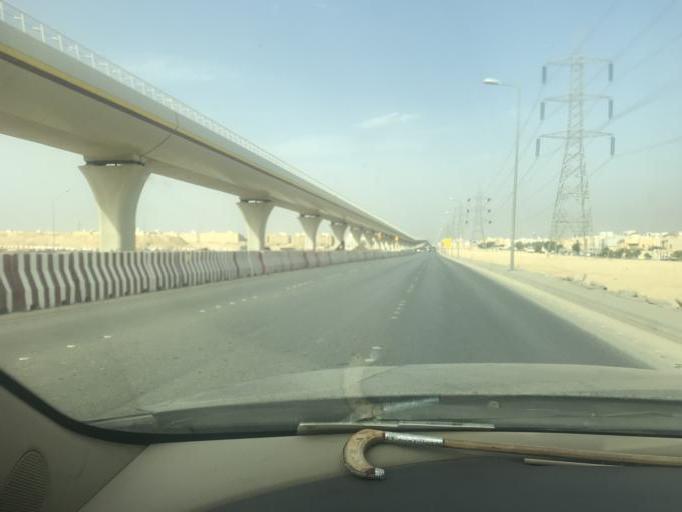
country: SA
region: Ar Riyad
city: Riyadh
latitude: 24.7876
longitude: 46.6638
